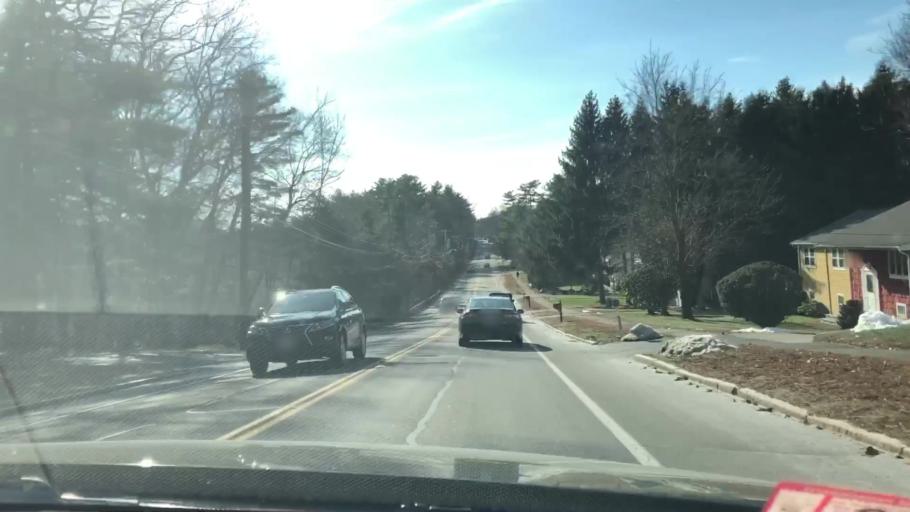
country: US
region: Massachusetts
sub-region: Norfolk County
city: Walpole
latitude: 42.1389
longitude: -71.2361
